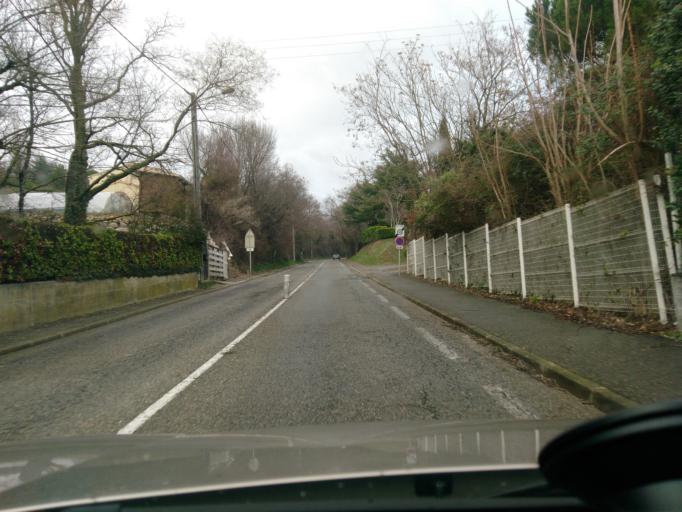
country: FR
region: Rhone-Alpes
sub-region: Departement de la Drome
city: Montelimar
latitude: 44.5736
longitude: 4.7605
